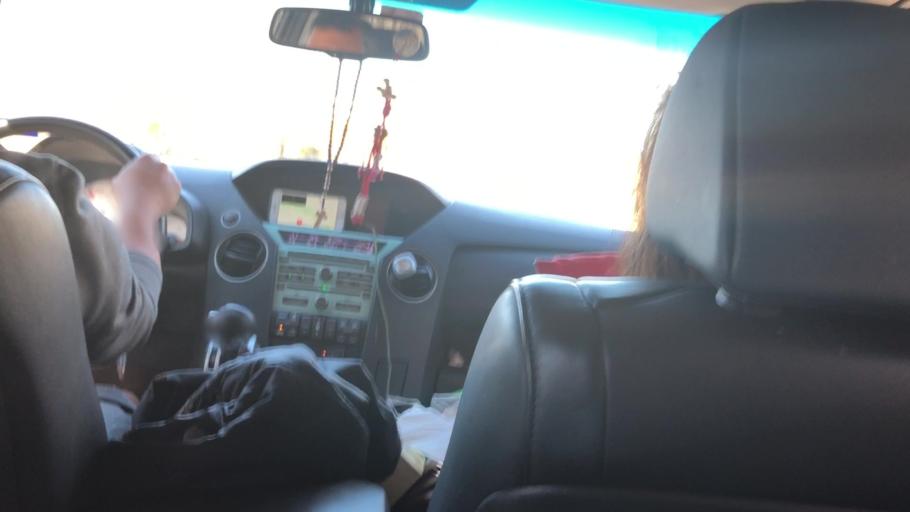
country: US
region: Louisiana
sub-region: Saint John the Baptist Parish
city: Montegut
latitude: 30.1043
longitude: -90.4923
